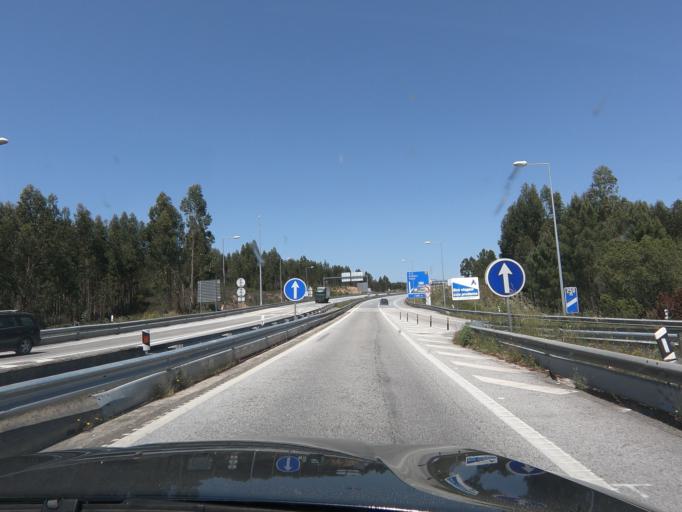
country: PT
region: Santarem
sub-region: Entroncamento
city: Entroncamento
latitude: 39.4901
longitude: -8.4468
